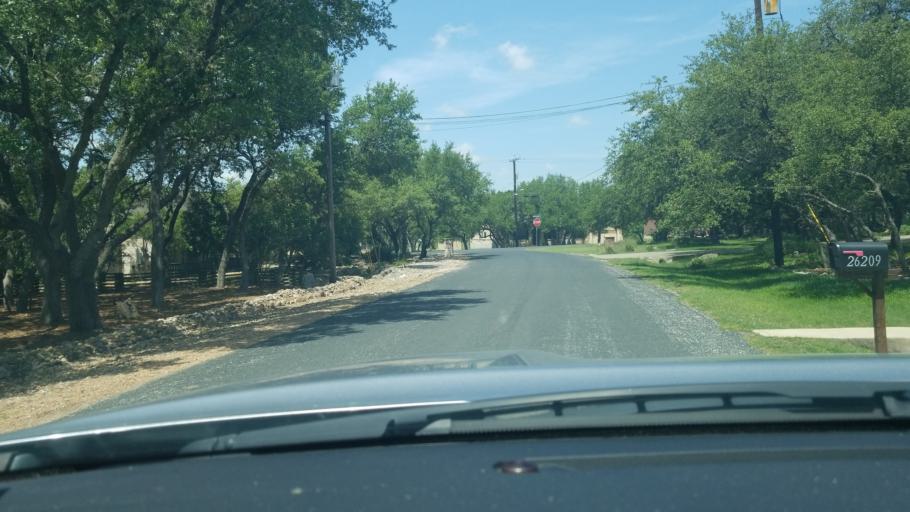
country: US
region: Texas
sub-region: Bexar County
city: Timberwood Park
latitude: 29.6895
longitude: -98.4885
